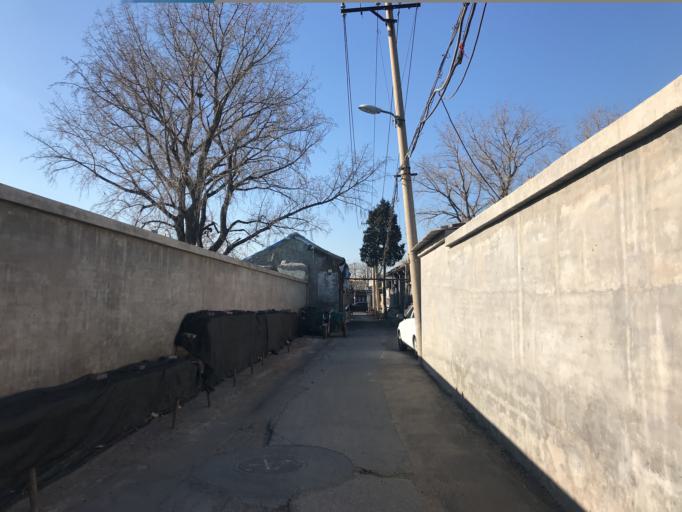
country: CN
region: Beijing
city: Beijing
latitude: 39.8907
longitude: 116.3895
